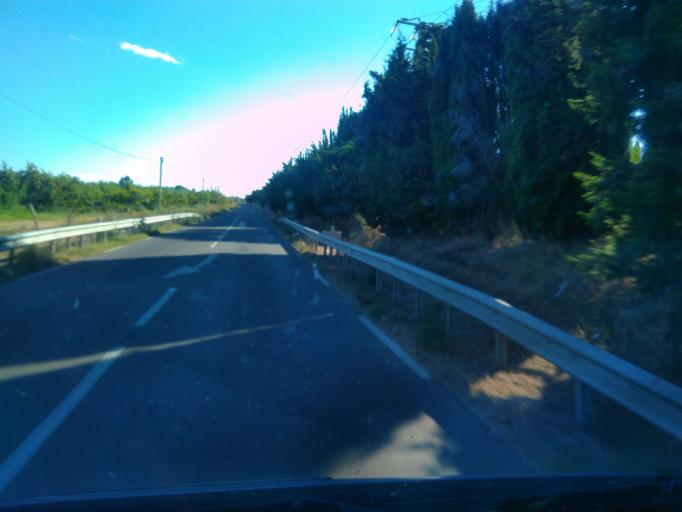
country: FR
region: Languedoc-Roussillon
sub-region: Departement du Gard
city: Saint-Gilles
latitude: 43.6657
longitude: 4.3689
